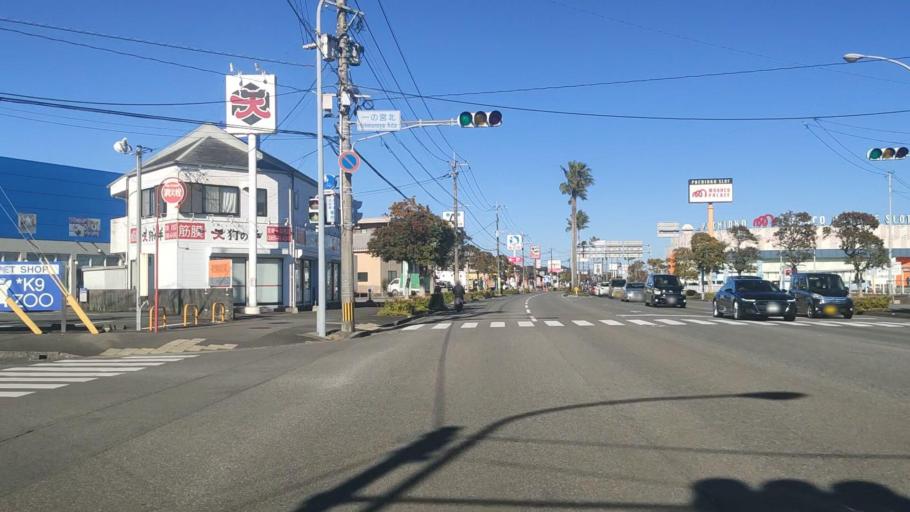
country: JP
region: Miyazaki
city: Miyazaki-shi
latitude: 31.9100
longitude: 131.4471
